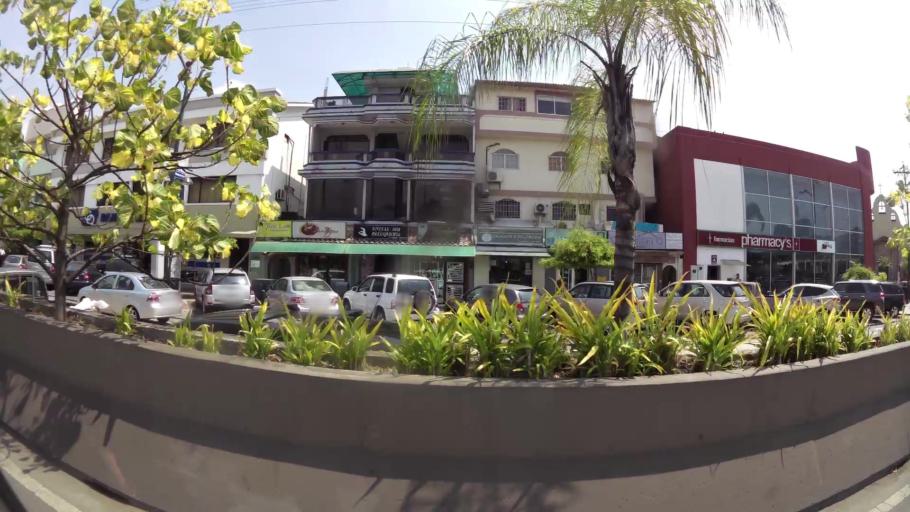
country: EC
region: Guayas
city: Eloy Alfaro
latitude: -2.1462
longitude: -79.8643
